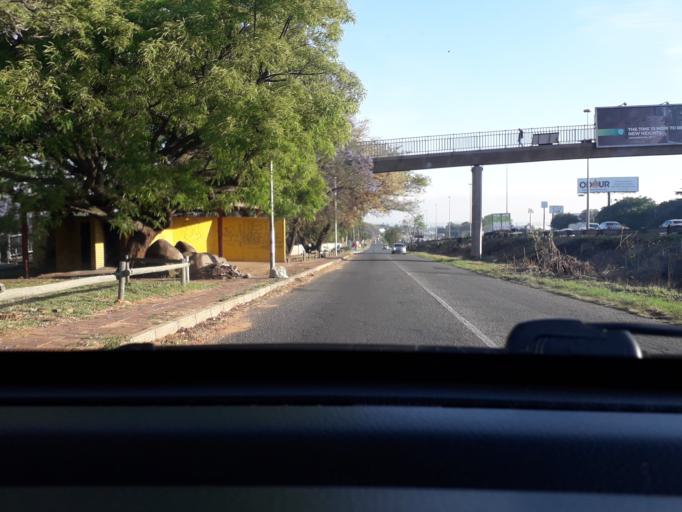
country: ZA
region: Gauteng
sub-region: City of Johannesburg Metropolitan Municipality
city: Modderfontein
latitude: -26.0832
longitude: 28.0864
